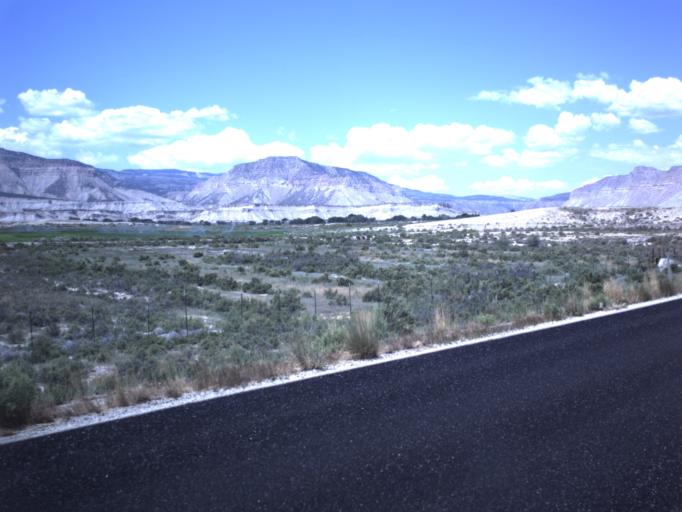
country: US
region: Utah
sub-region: Emery County
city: Ferron
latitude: 39.0594
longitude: -111.1286
